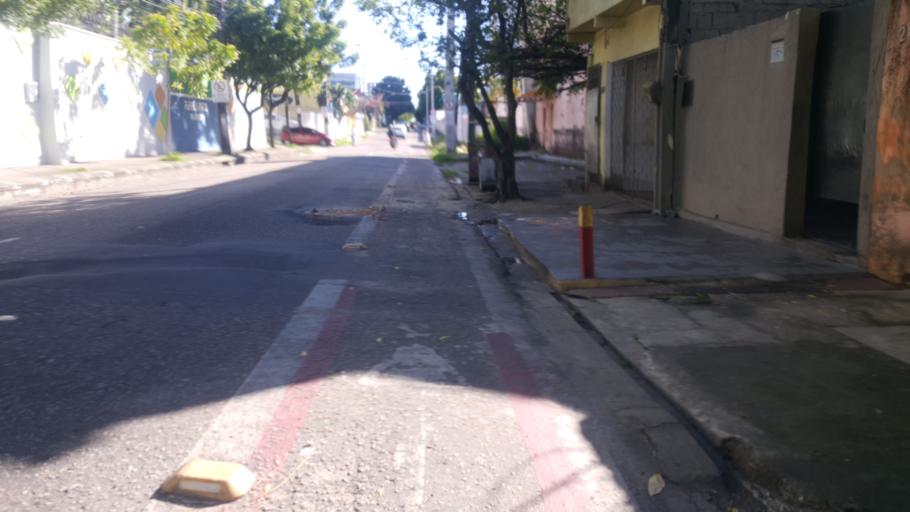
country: BR
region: Ceara
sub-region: Fortaleza
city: Fortaleza
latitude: -3.7434
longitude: -38.5336
